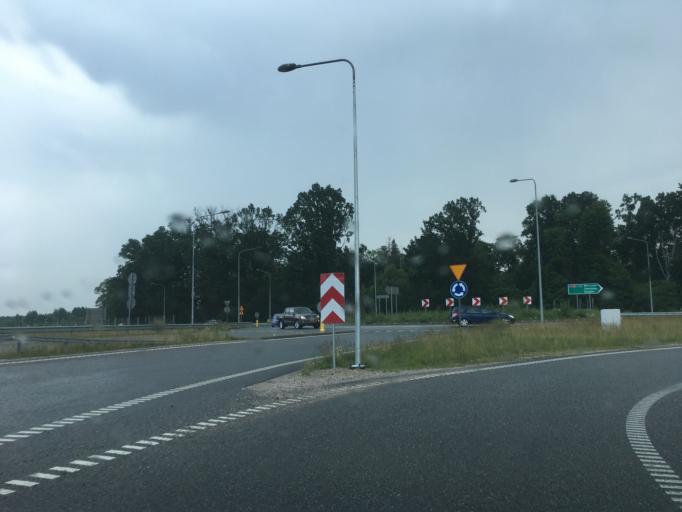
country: PL
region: Lodz Voivodeship
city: Zabia Wola
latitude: 52.0525
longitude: 20.7157
